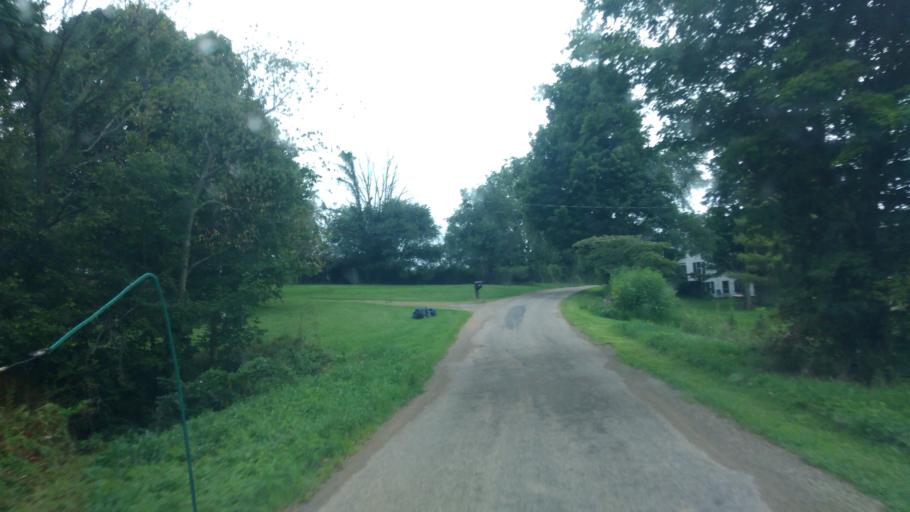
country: US
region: Ohio
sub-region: Knox County
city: Gambier
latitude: 40.3041
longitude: -82.3118
